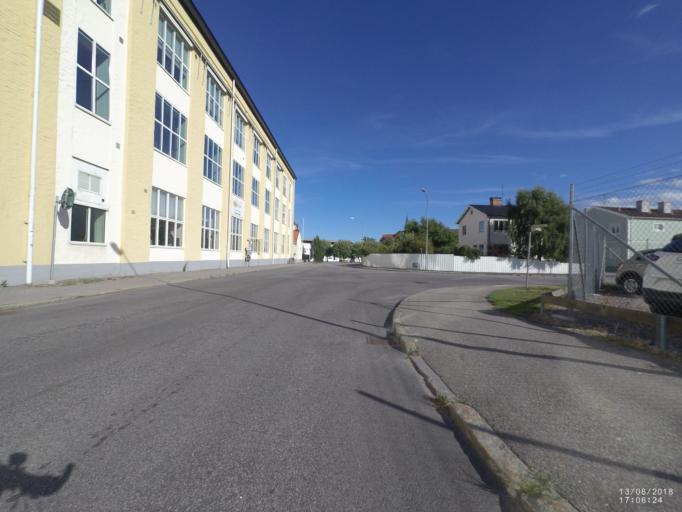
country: SE
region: Soedermanland
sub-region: Nykopings Kommun
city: Nykoping
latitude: 58.7532
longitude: 16.9934
